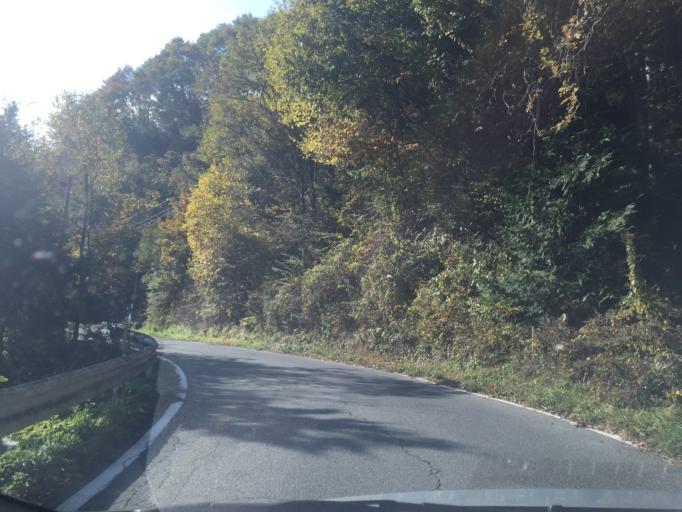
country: JP
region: Nagano
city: Iida
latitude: 35.3737
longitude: 137.7000
